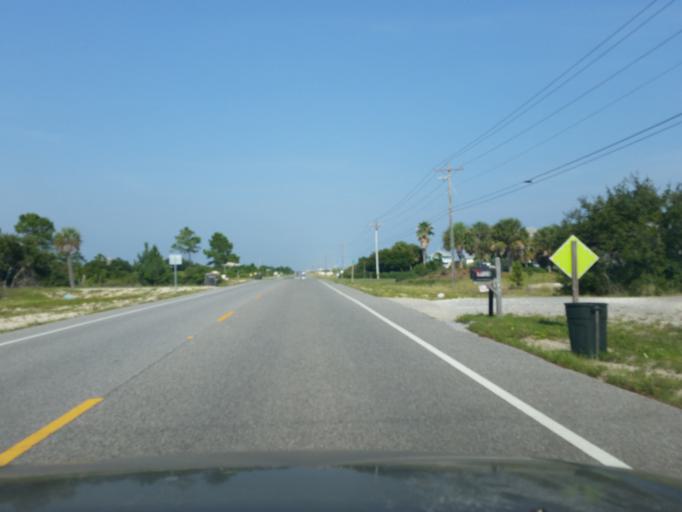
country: US
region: Alabama
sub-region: Mobile County
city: Dauphin Island
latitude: 30.2312
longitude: -87.9917
